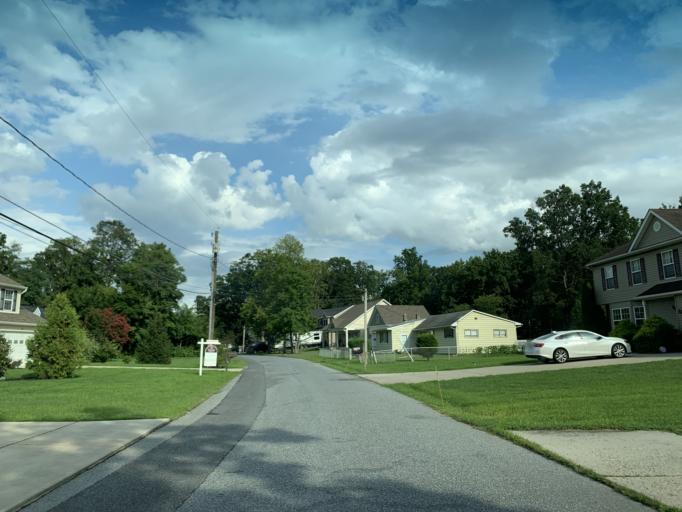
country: US
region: Maryland
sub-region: Baltimore County
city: Essex
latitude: 39.2904
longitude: -76.4388
